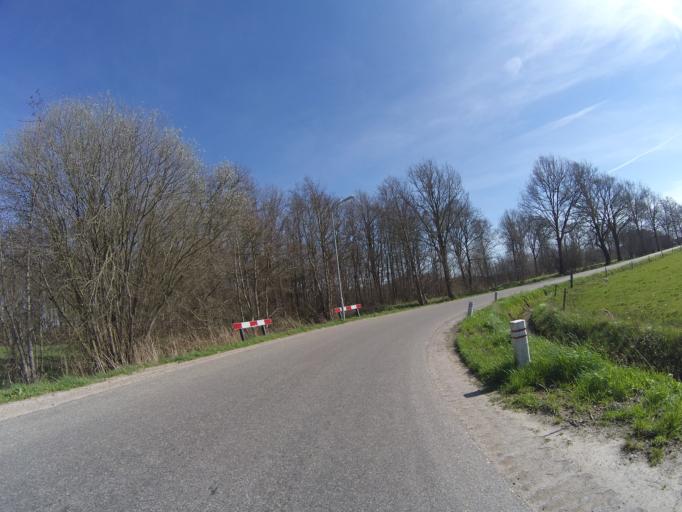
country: NL
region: Gelderland
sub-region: Gemeente Barneveld
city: Zwartebroek
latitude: 52.1950
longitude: 5.4989
